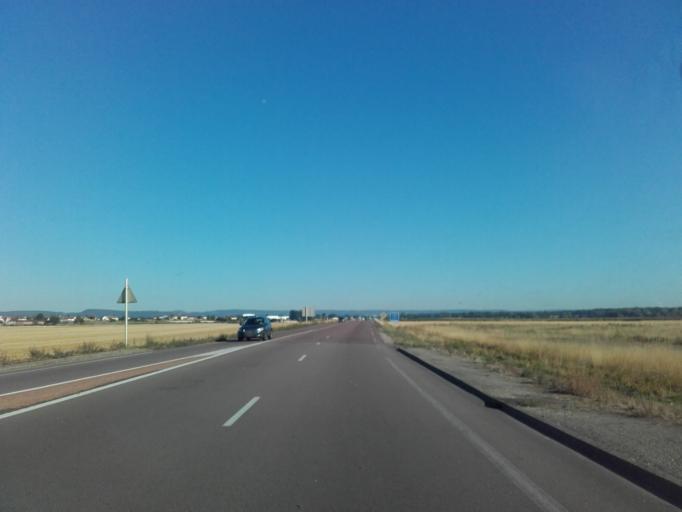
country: FR
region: Bourgogne
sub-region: Departement de Saone-et-Loire
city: Champforgeuil
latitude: 46.8308
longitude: 4.8249
